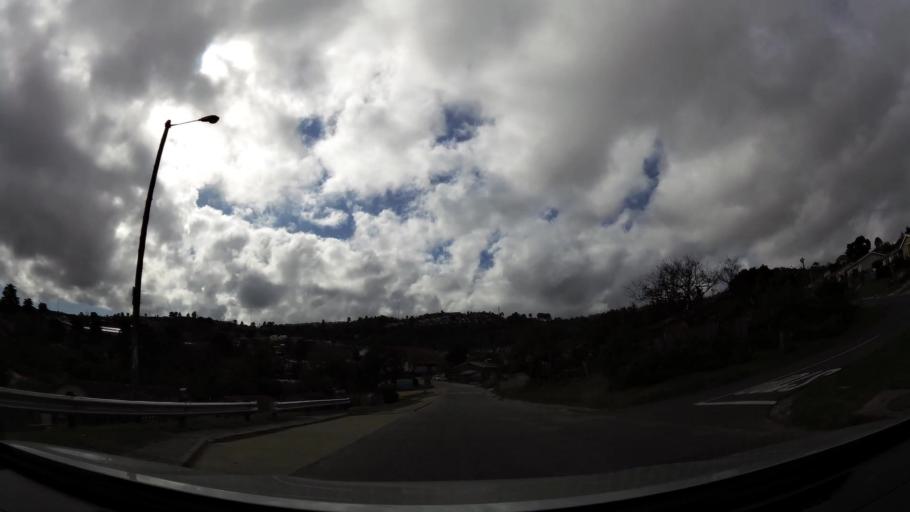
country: ZA
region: Western Cape
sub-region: Eden District Municipality
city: Knysna
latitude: -34.0499
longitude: 23.0966
